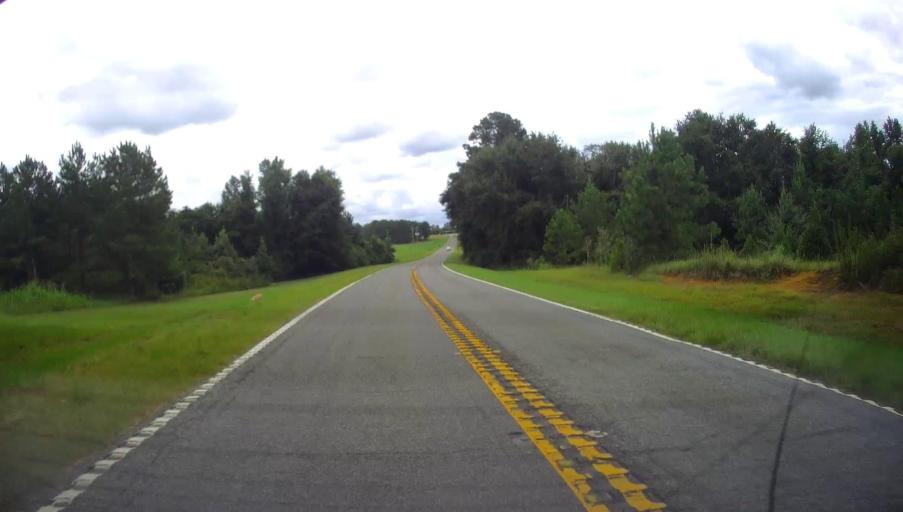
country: US
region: Georgia
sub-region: Dooly County
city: Unadilla
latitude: 32.2816
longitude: -83.8221
